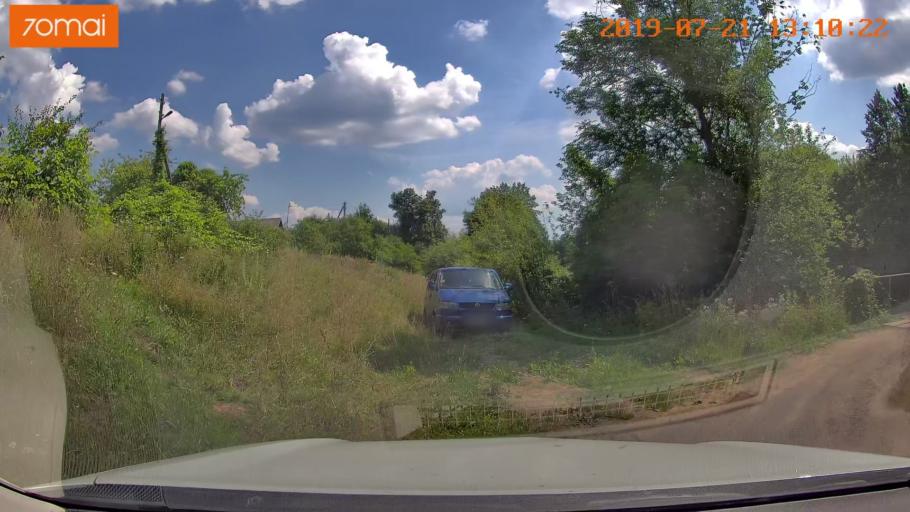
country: BY
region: Grodnenskaya
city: Lyubcha
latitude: 53.8253
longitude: 26.0480
